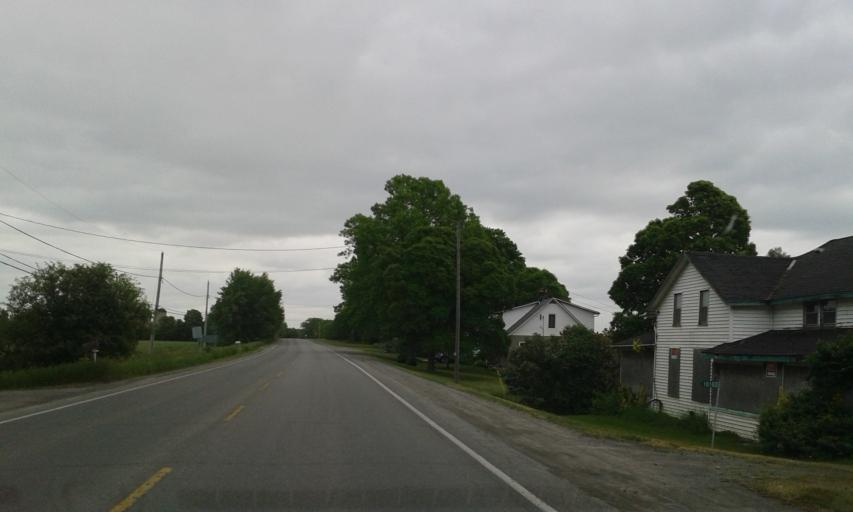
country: CA
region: Ontario
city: Prince Edward
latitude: 43.9552
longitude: -77.3288
